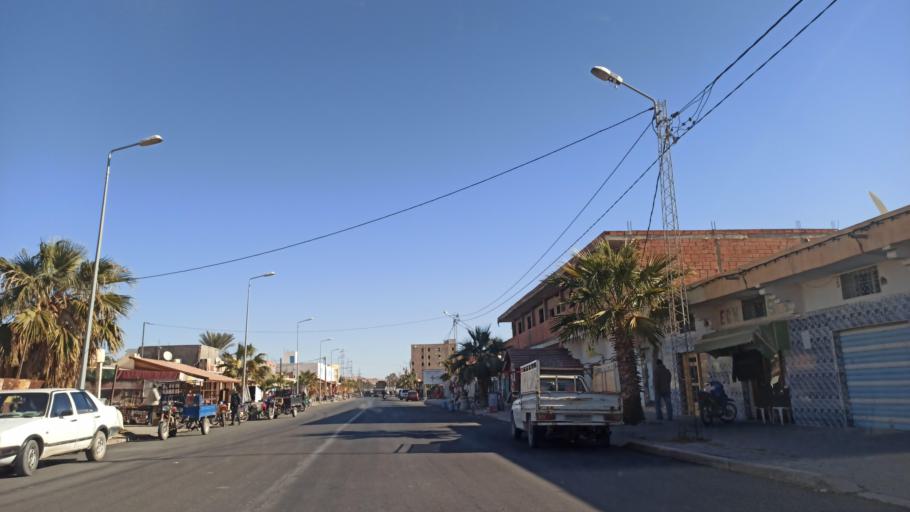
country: TN
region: Gafsa
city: Al Metlaoui
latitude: 34.3129
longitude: 8.3873
